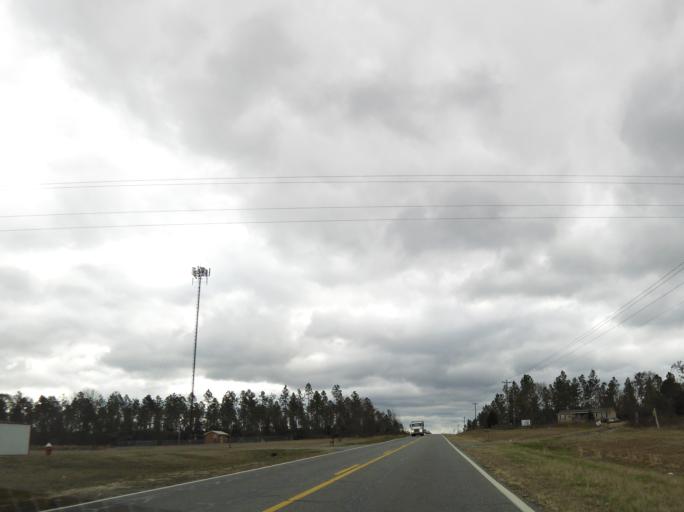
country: US
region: Georgia
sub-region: Bleckley County
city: Cochran
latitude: 32.4095
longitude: -83.3447
